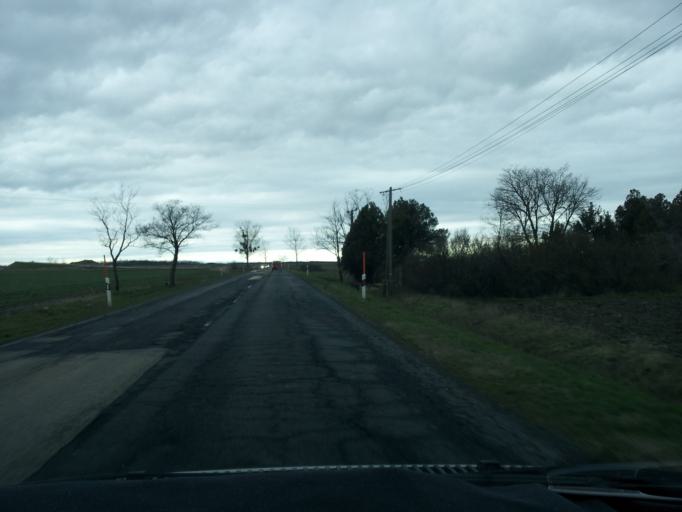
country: HU
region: Gyor-Moson-Sopron
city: Beled
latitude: 47.4782
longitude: 17.1533
